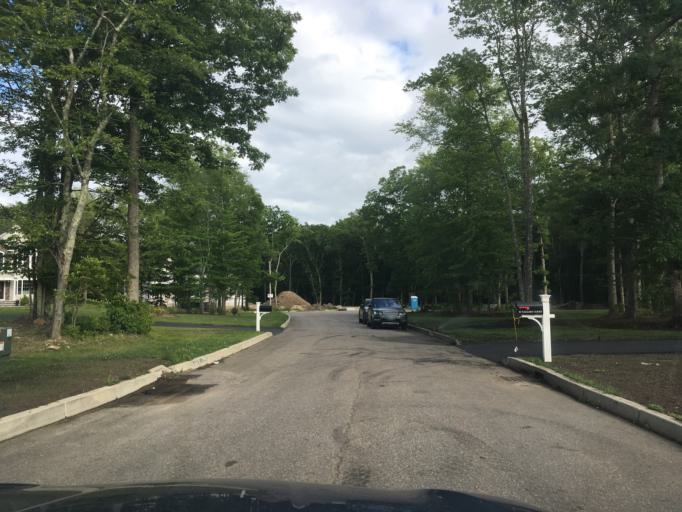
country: US
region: Rhode Island
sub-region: Washington County
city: Exeter
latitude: 41.6029
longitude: -71.5377
